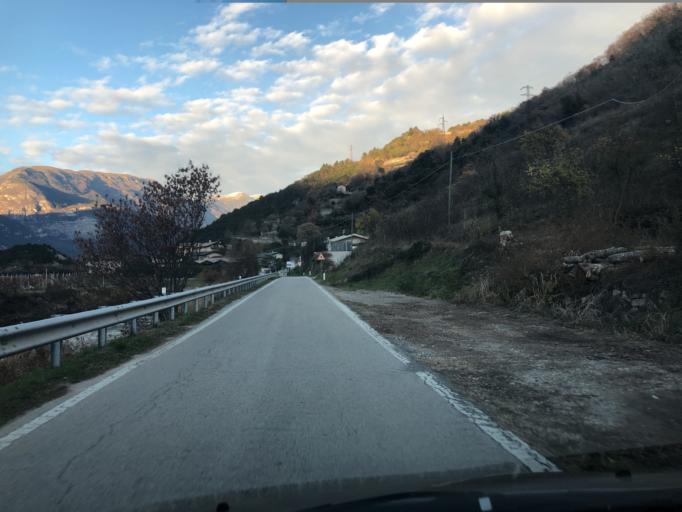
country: IT
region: Trentino-Alto Adige
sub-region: Provincia di Trento
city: Pietramurata
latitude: 46.0141
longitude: 10.9587
